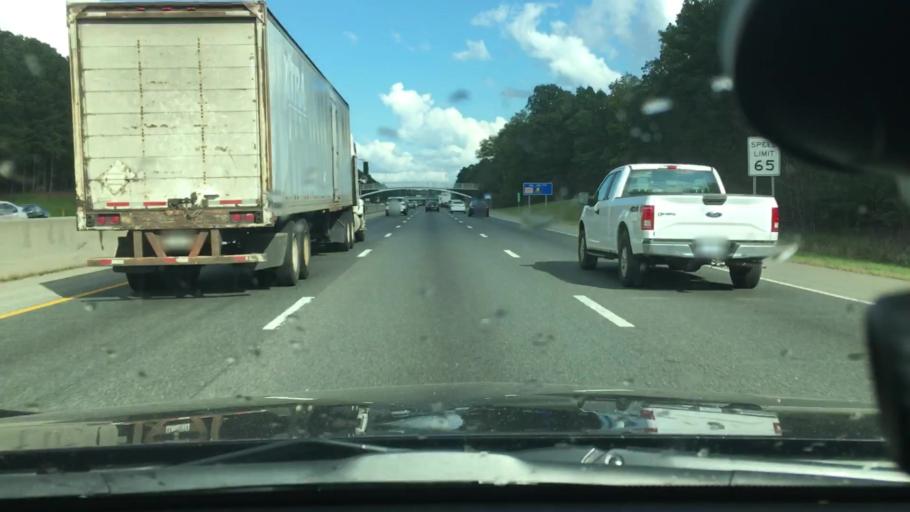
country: US
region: North Carolina
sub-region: Durham County
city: Durham
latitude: 35.9064
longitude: -78.9480
